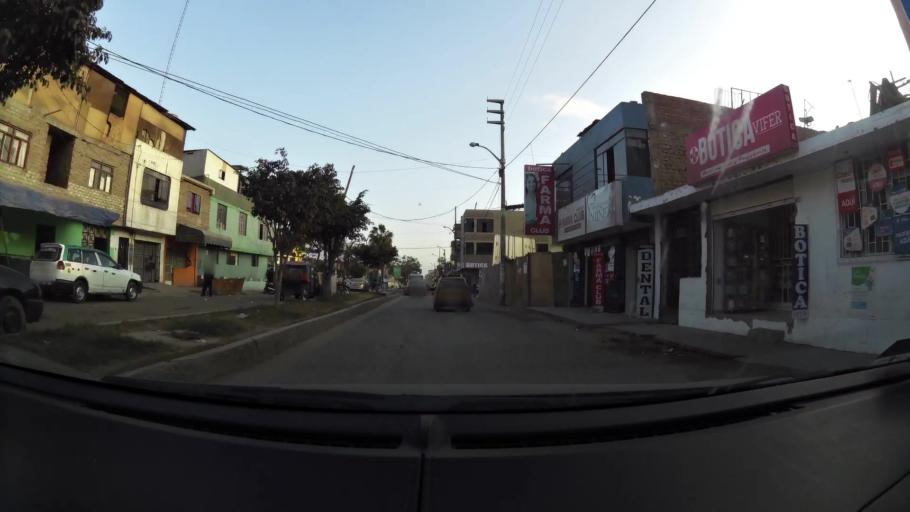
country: PE
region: La Libertad
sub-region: Provincia de Trujillo
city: El Porvenir
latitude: -8.0784
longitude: -78.9997
